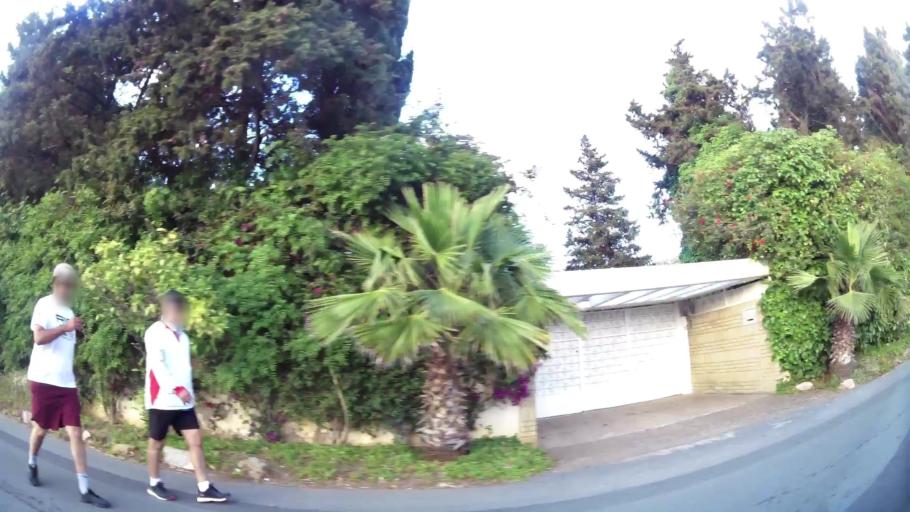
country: MA
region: Rabat-Sale-Zemmour-Zaer
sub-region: Rabat
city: Rabat
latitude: 33.9733
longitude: -6.8414
